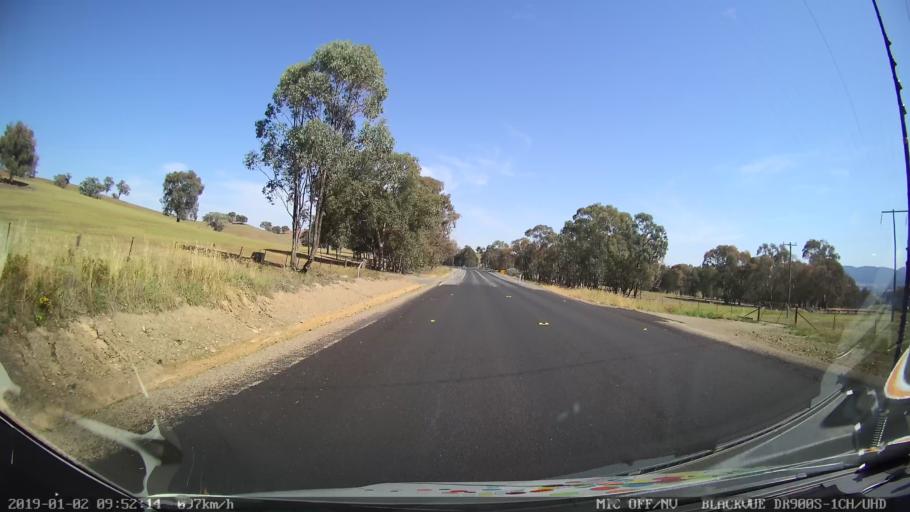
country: AU
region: New South Wales
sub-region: Tumut Shire
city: Tumut
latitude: -35.2633
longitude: 148.2081
